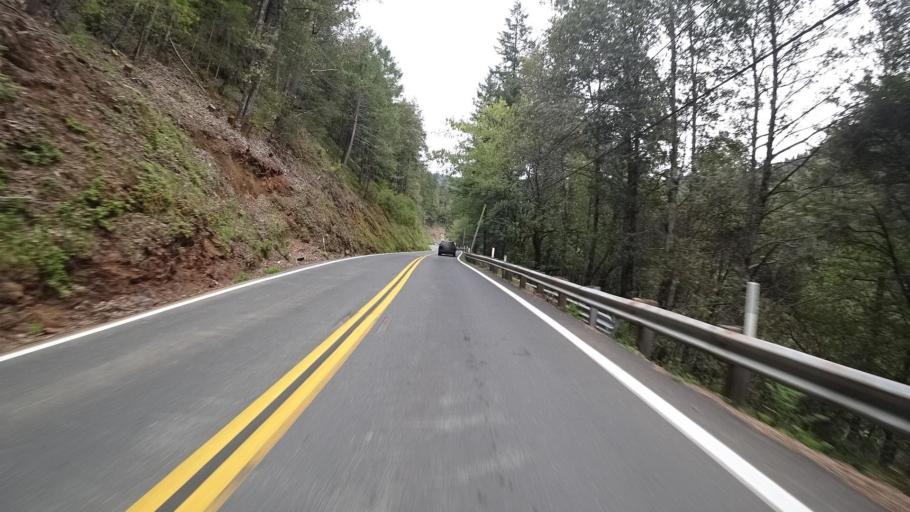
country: US
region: California
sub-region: Humboldt County
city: Willow Creek
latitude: 41.0127
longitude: -123.6369
